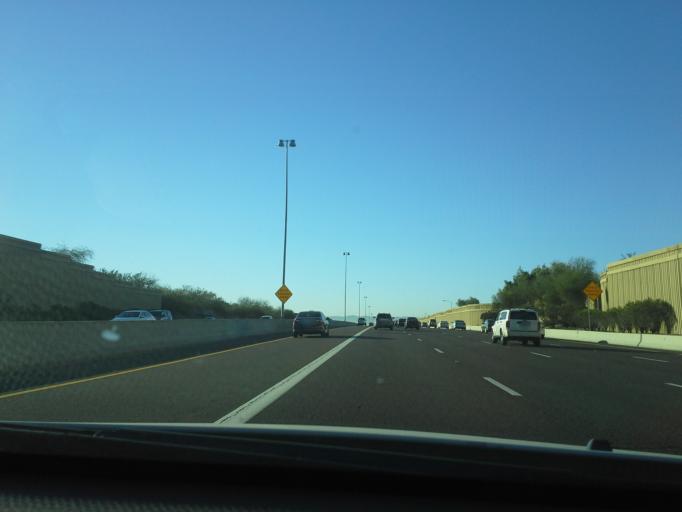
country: US
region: Arizona
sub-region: Maricopa County
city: Paradise Valley
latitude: 33.5467
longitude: -112.0395
